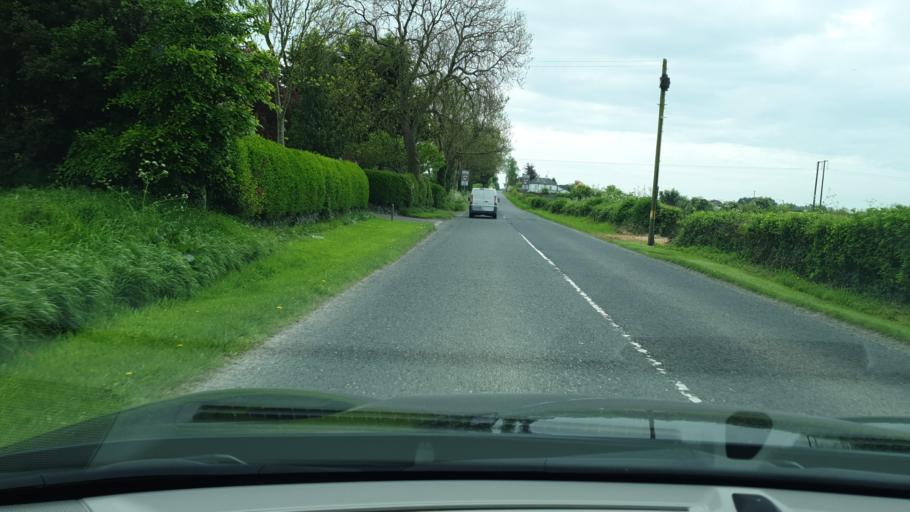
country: IE
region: Leinster
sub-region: An Mhi
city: Navan
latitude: 53.7114
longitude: -6.6906
